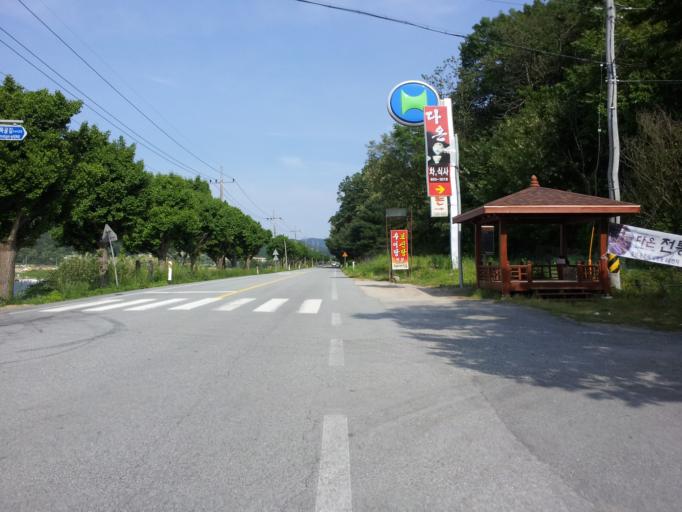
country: KR
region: Chungcheongnam-do
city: Gongju
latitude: 36.4447
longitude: 127.1840
